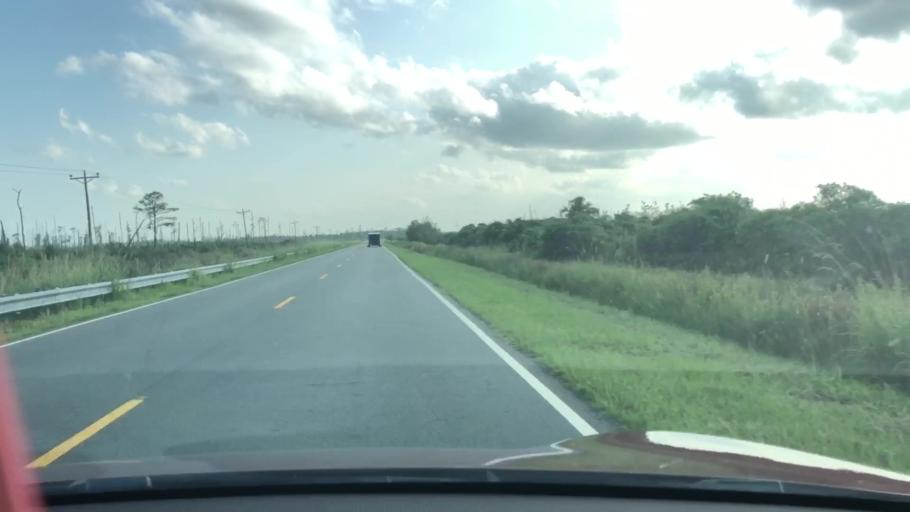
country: US
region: North Carolina
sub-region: Dare County
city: Wanchese
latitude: 35.6257
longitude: -75.7847
